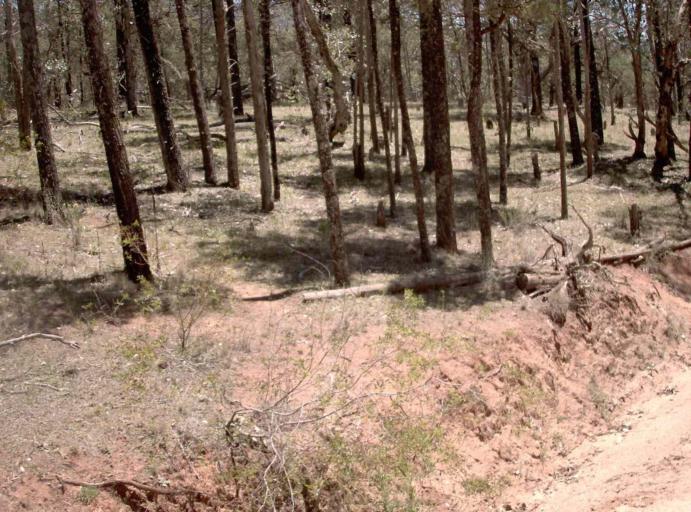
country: AU
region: New South Wales
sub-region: Snowy River
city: Jindabyne
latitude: -36.8909
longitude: 148.4214
